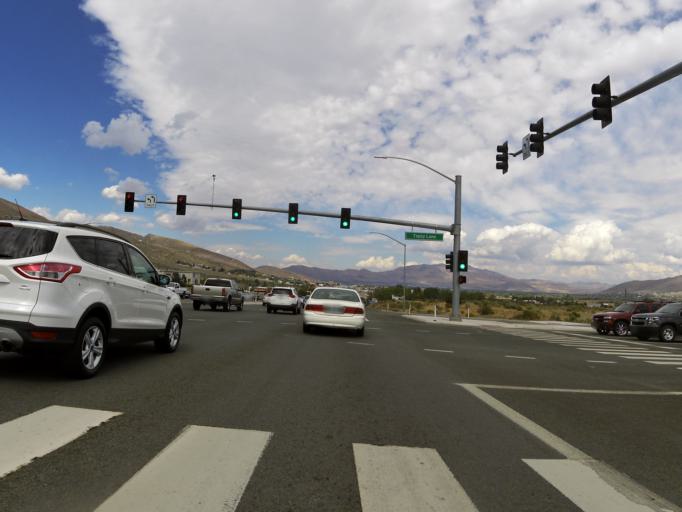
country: US
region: Nevada
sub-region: Douglas County
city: Indian Hills
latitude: 39.1102
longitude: -119.7736
